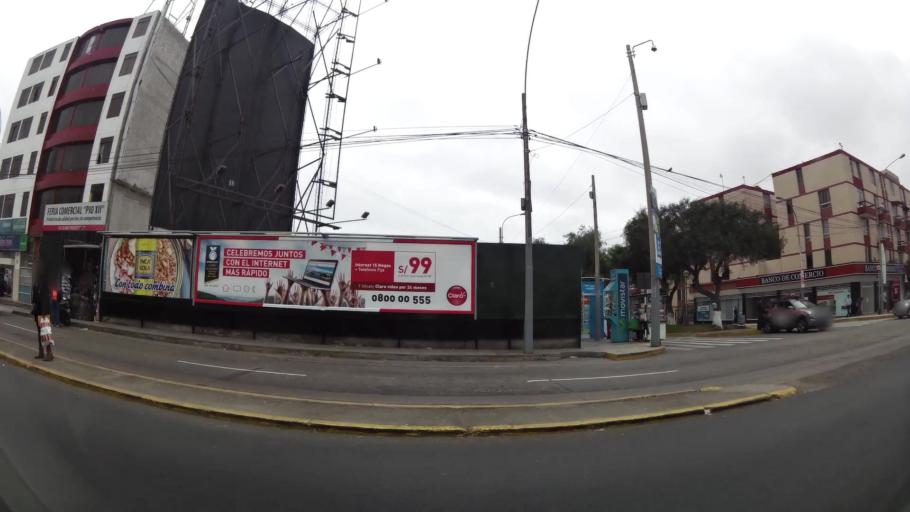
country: PE
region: Callao
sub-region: Callao
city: Callao
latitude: -12.0645
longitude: -77.0973
